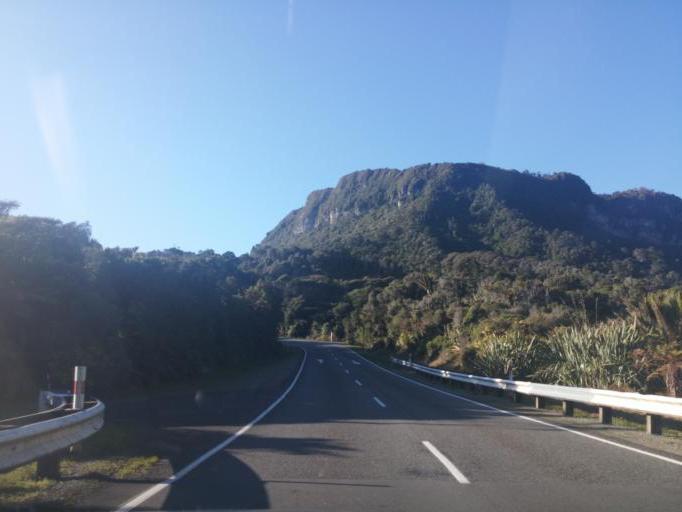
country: NZ
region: West Coast
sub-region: Grey District
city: Greymouth
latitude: -42.1008
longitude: 171.3413
